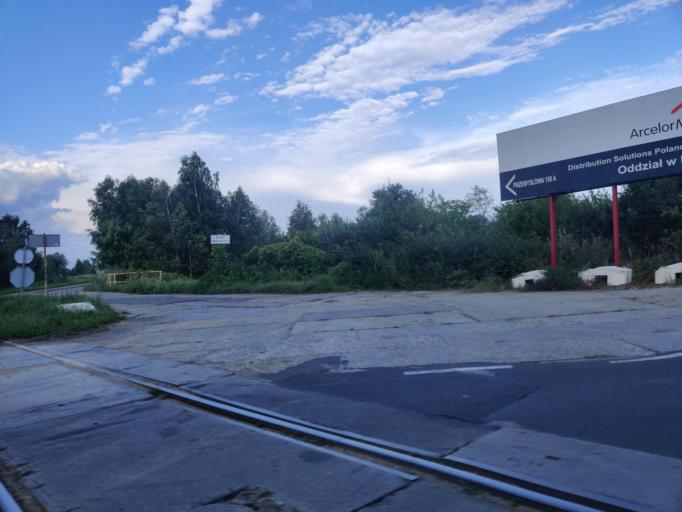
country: PL
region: Greater Poland Voivodeship
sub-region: Konin
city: Konin
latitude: 52.2766
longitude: 18.2665
